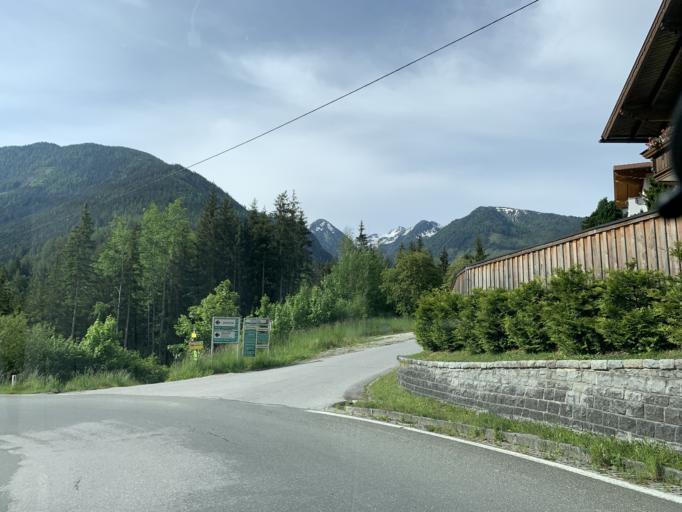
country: AT
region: Styria
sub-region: Politischer Bezirk Liezen
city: Schladming
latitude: 47.3729
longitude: 13.6728
